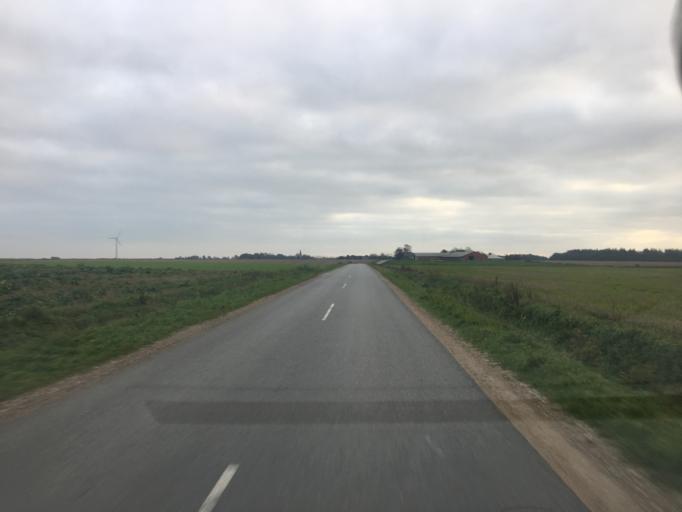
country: DE
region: Schleswig-Holstein
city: Aventoft
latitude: 54.9845
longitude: 8.7548
